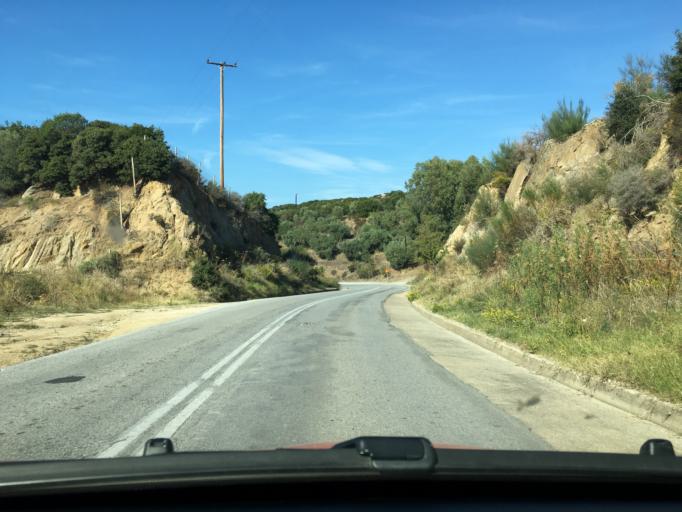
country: GR
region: Central Macedonia
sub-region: Nomos Chalkidikis
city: Ouranoupolis
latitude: 40.3354
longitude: 23.9727
